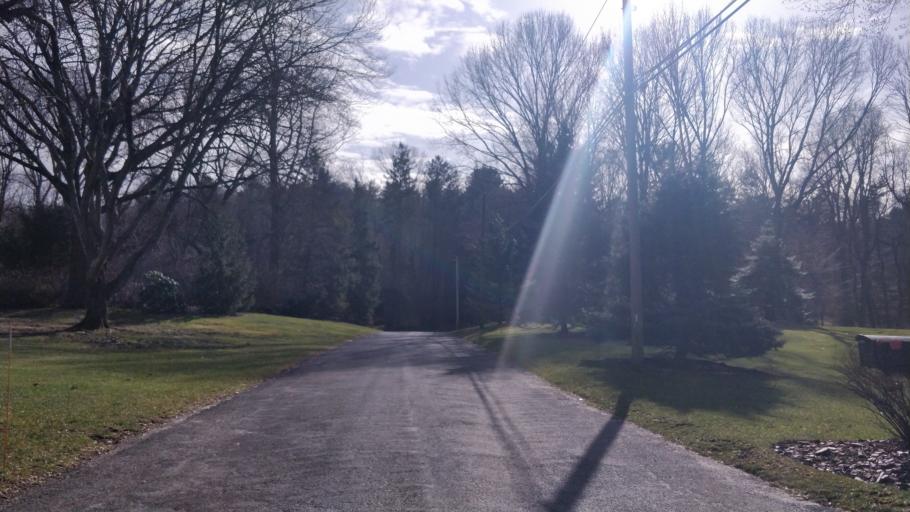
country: US
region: New York
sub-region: Nassau County
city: Oyster Bay
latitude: 40.8716
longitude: -73.5558
